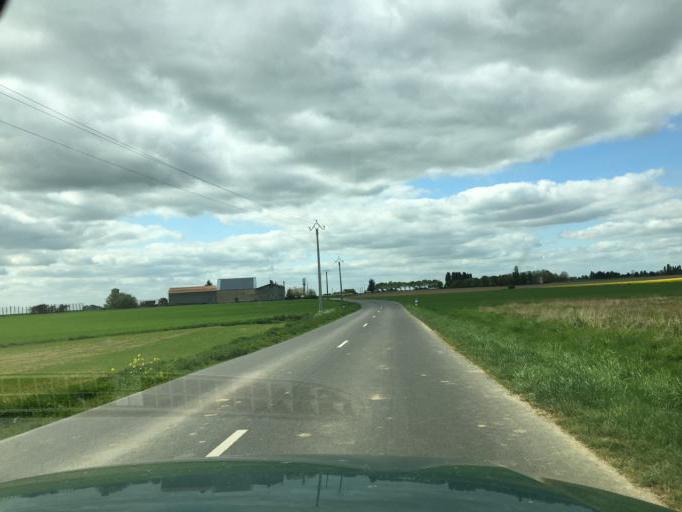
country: FR
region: Centre
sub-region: Departement du Loir-et-Cher
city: Oucques
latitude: 47.8155
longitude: 1.4160
